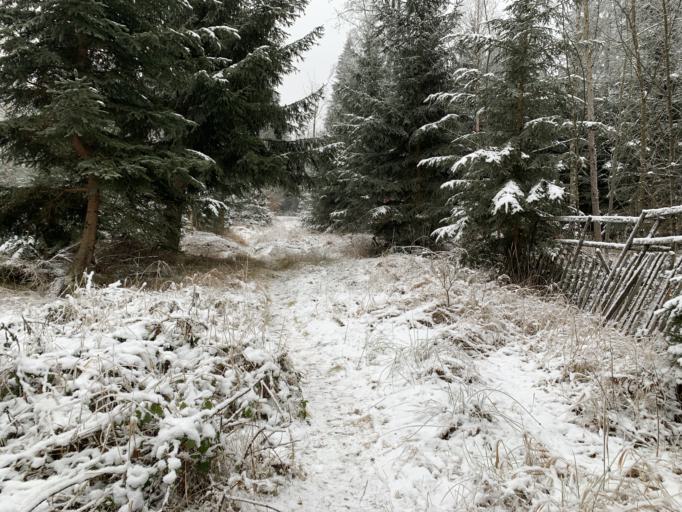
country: CZ
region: Central Bohemia
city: Rozmital pod Tremsinem
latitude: 49.5788
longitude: 13.8152
